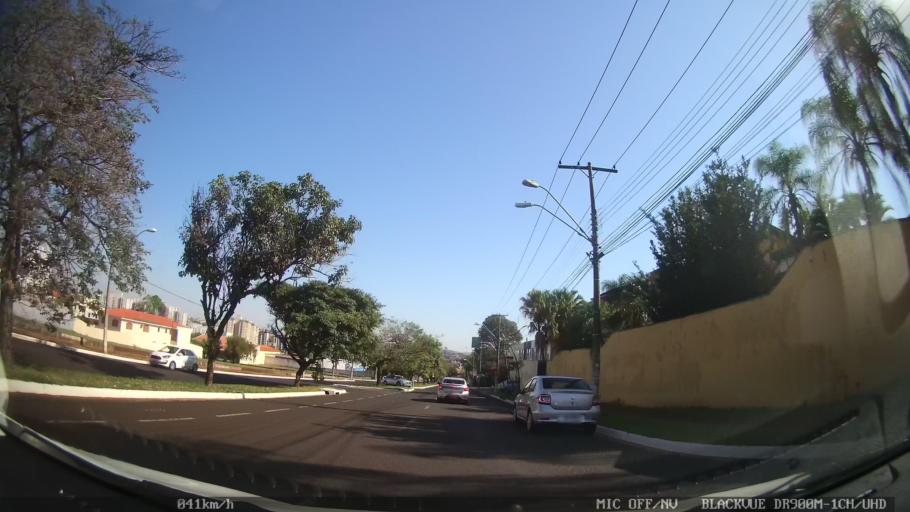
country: BR
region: Sao Paulo
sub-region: Ribeirao Preto
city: Ribeirao Preto
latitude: -21.1975
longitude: -47.8186
